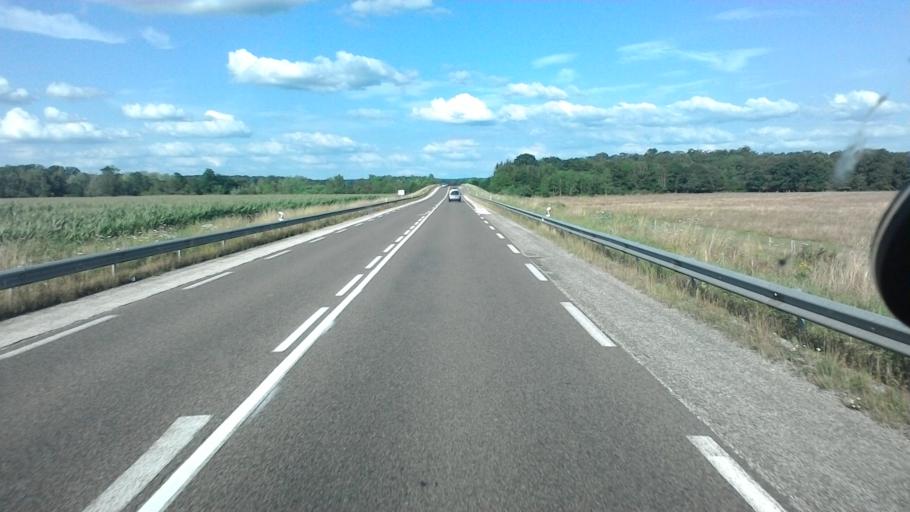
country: FR
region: Franche-Comte
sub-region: Departement de la Haute-Saone
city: Saint-Sauveur
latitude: 47.7853
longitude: 6.3809
